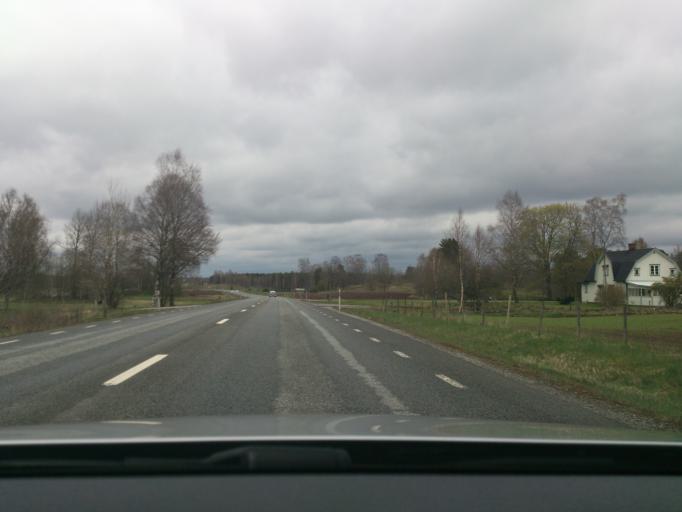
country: SE
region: Vaestra Goetaland
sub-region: Ulricehamns Kommun
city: Ulricehamn
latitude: 57.9646
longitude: 13.5265
